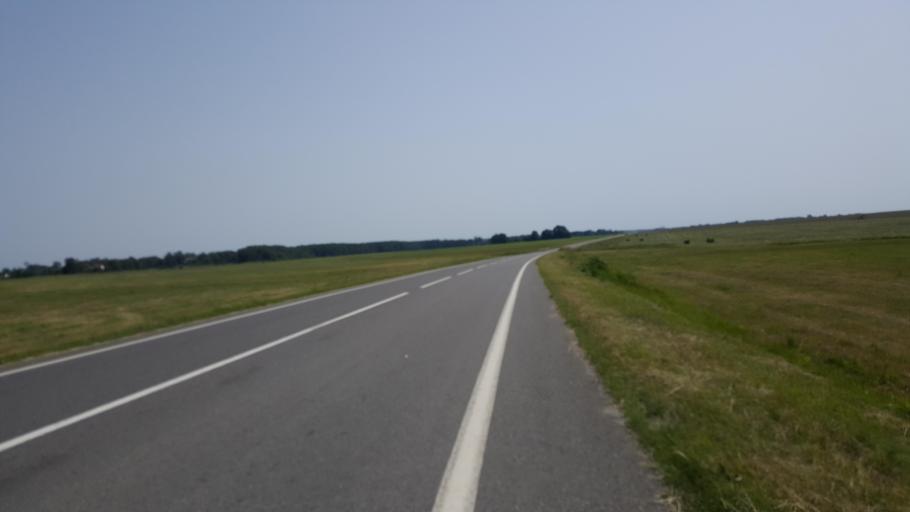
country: BY
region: Brest
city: Kamyanyets
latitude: 52.4549
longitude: 23.8336
